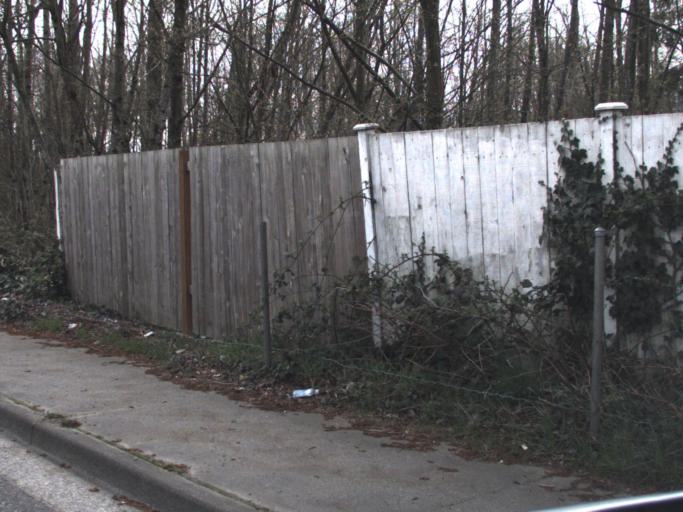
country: US
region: Washington
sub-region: King County
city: Lea Hill
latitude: 47.3654
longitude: -122.1823
